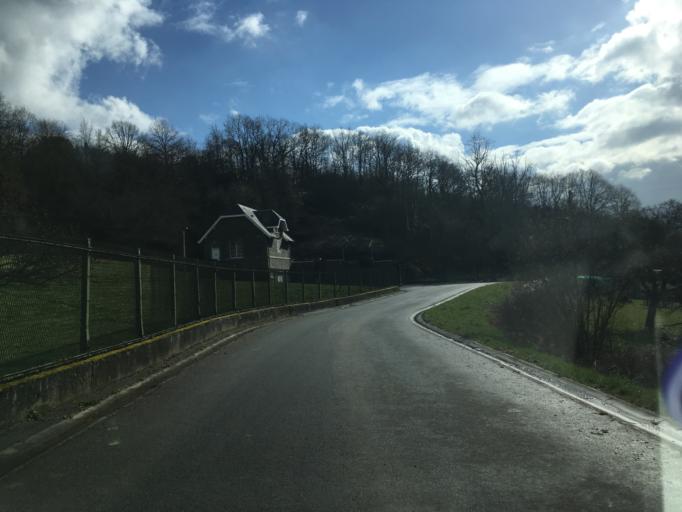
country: BE
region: Wallonia
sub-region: Province de Namur
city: Couvin
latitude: 50.0938
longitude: 4.5904
